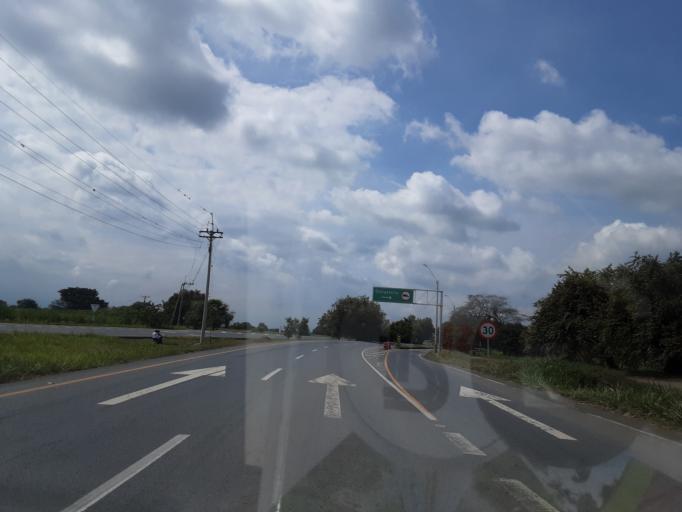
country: CO
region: Valle del Cauca
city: Guacari
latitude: 3.7294
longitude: -76.3224
